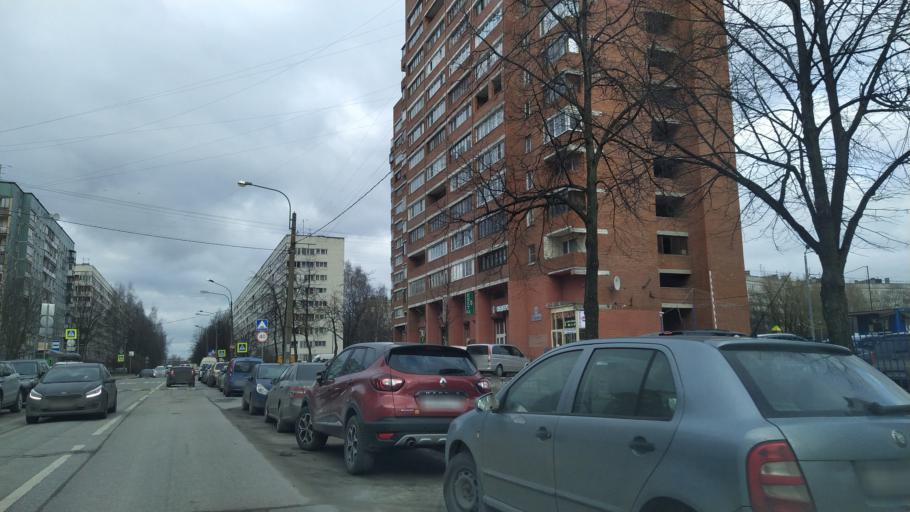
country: RU
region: Leningrad
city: Parnas
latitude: 60.0496
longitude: 30.3693
